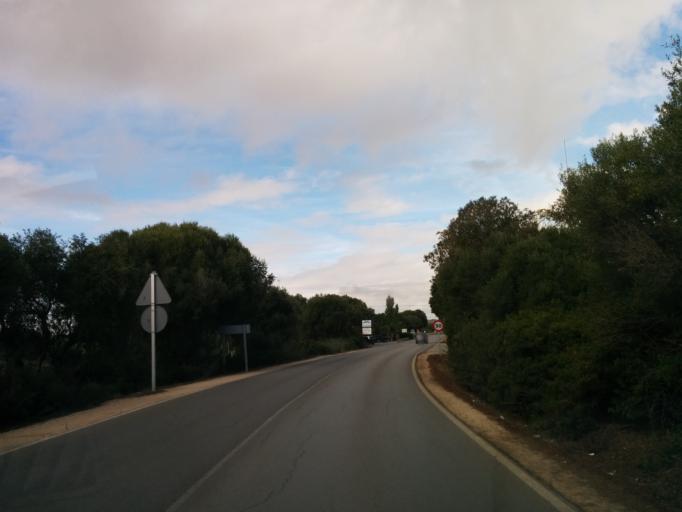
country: ES
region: Andalusia
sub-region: Provincia de Cadiz
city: Vejer de la Frontera
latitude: 36.2027
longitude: -6.0353
